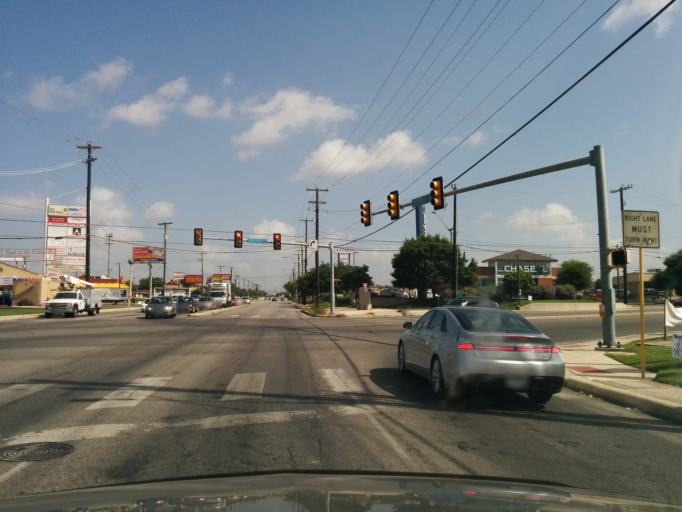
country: US
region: Texas
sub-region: Bexar County
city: Leon Valley
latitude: 29.5235
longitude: -98.5997
